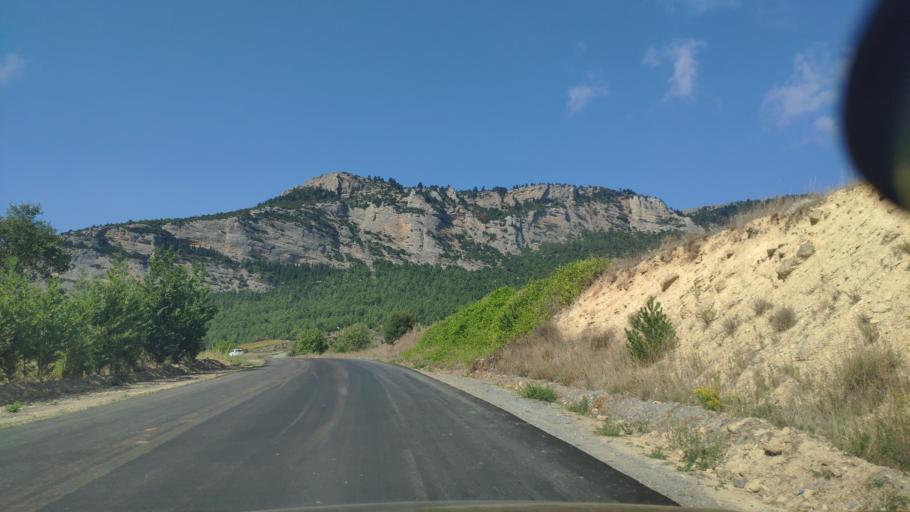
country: GR
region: Peloponnese
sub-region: Nomos Korinthias
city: Xylokastro
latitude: 37.9382
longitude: 22.5469
